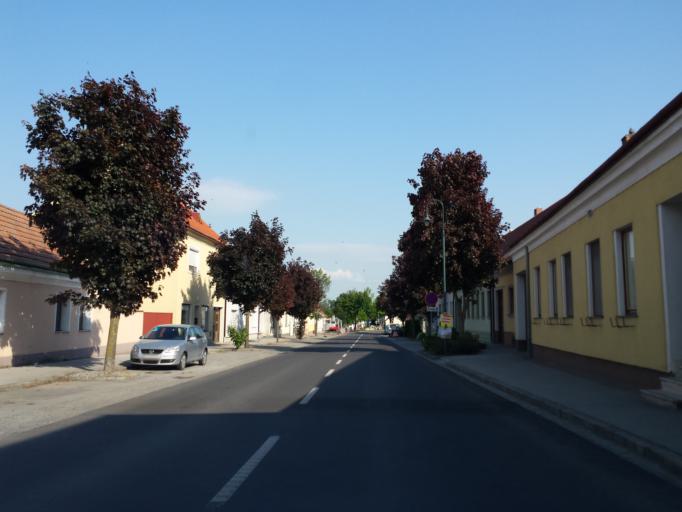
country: AT
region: Lower Austria
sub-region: Politischer Bezirk Ganserndorf
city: Angern an der March
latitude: 48.3779
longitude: 16.8305
